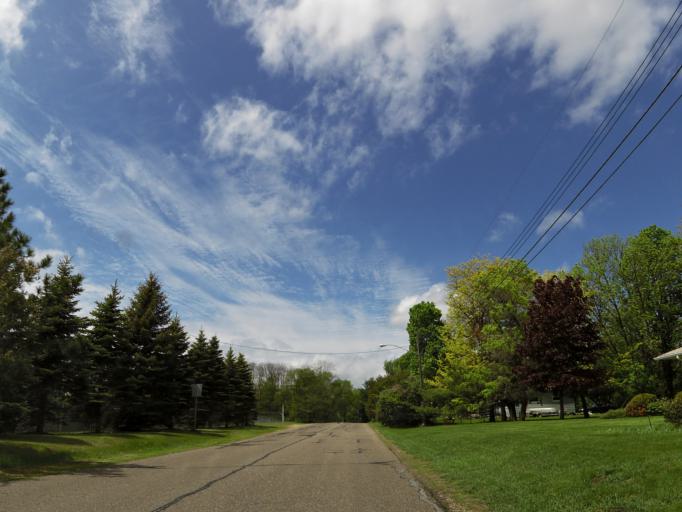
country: US
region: Wisconsin
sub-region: Saint Croix County
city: Hudson
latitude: 44.9813
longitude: -92.7393
